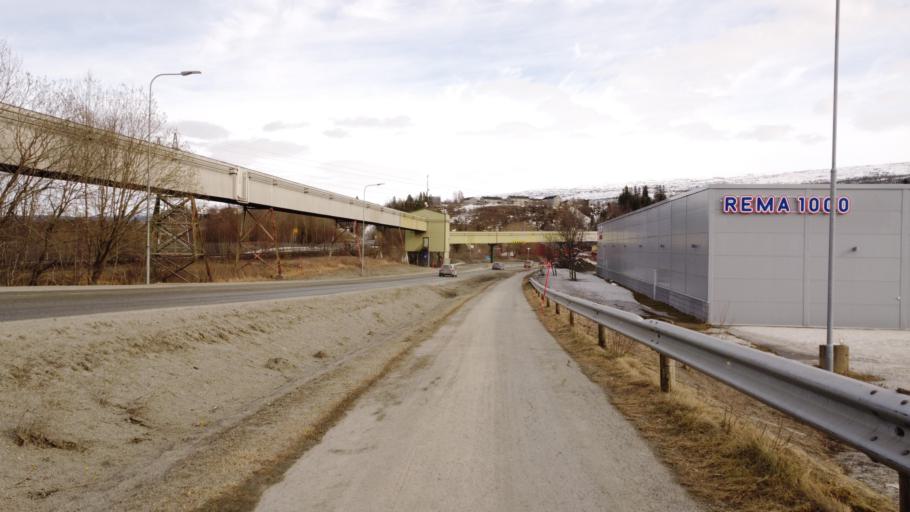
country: NO
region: Nordland
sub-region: Rana
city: Mo i Rana
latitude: 66.3228
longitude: 14.1665
